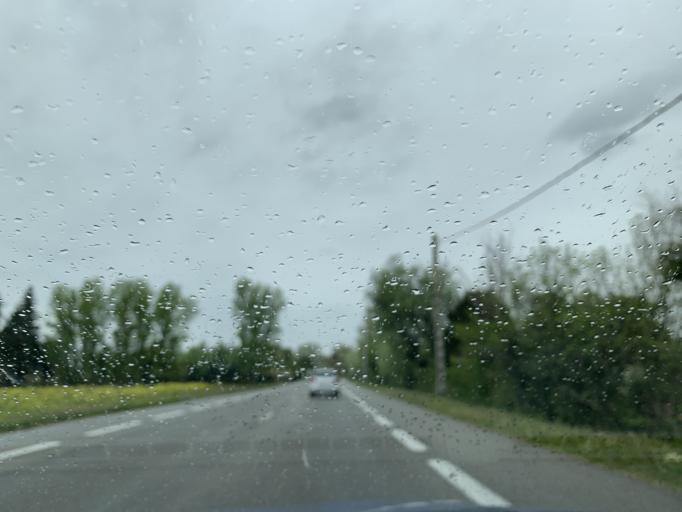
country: FR
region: Provence-Alpes-Cote d'Azur
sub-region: Departement du Vaucluse
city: Velleron
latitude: 43.9776
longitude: 5.0177
